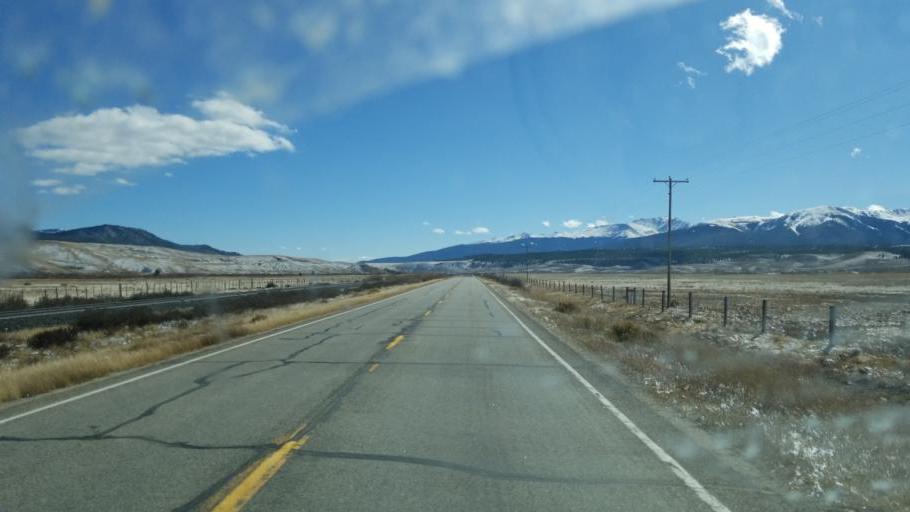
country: US
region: Colorado
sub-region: Lake County
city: Leadville
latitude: 39.1532
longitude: -106.3222
